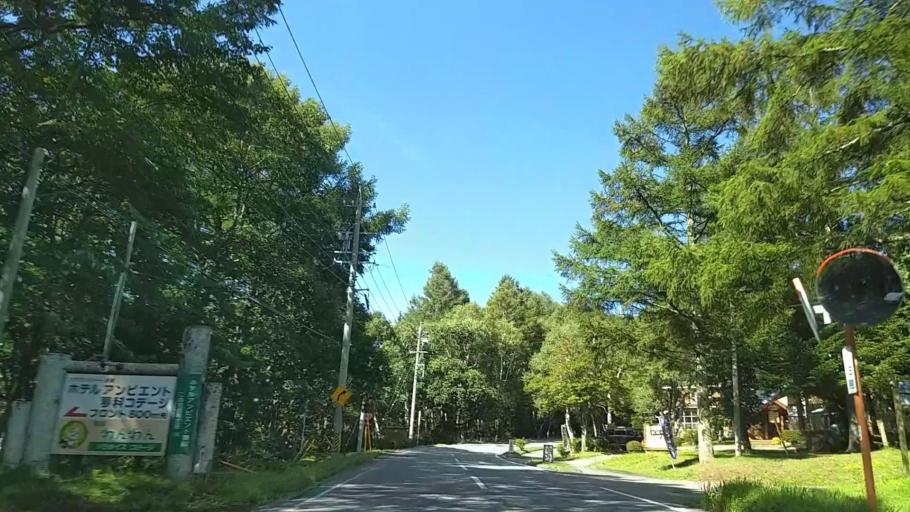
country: JP
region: Nagano
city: Chino
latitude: 36.1267
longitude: 138.2682
